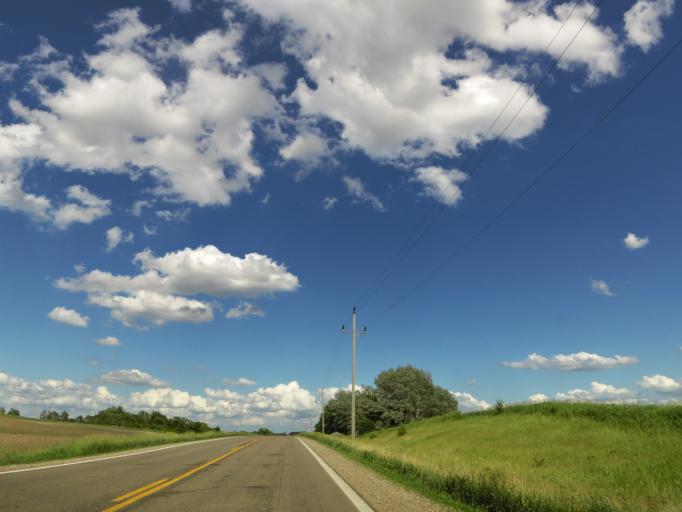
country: US
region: Minnesota
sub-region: Wright County
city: Cokato
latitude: 45.0657
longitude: -94.2139
